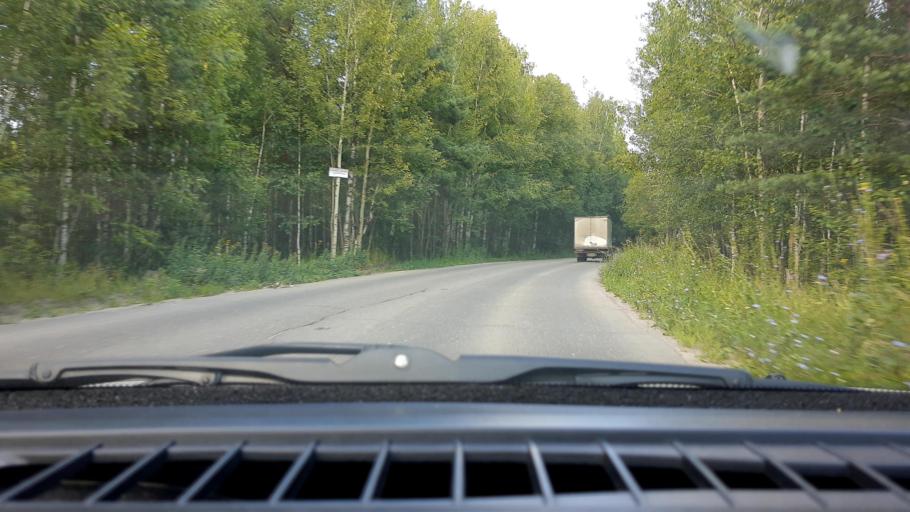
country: RU
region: Nizjnij Novgorod
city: Babino
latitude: 56.3165
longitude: 43.6236
